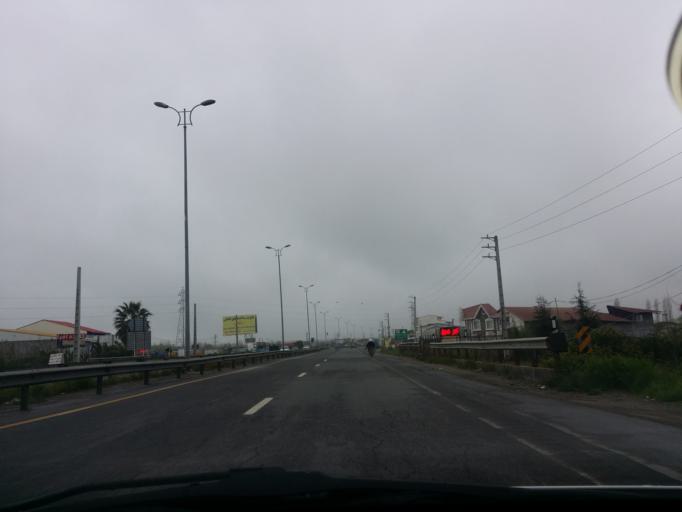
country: IR
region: Mazandaran
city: Tonekabon
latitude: 36.7963
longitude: 50.9054
